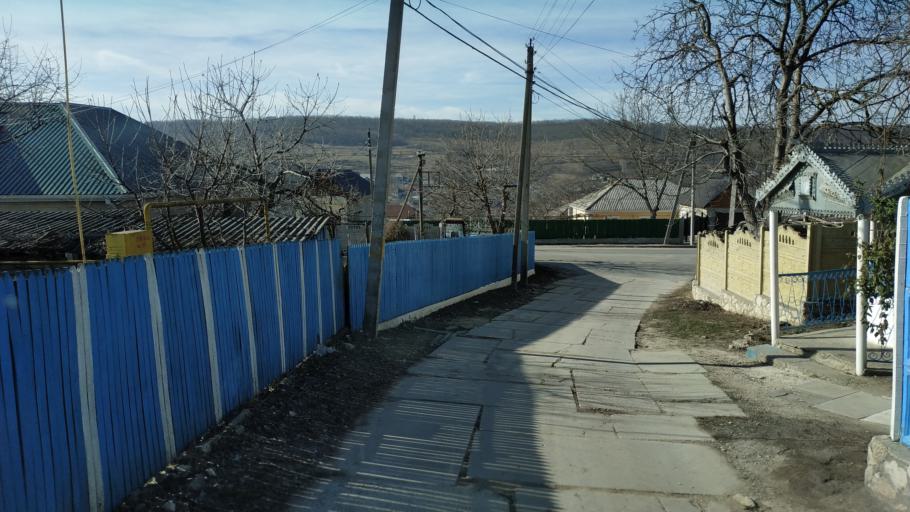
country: MD
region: Chisinau
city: Vatra
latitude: 47.0295
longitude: 28.6327
